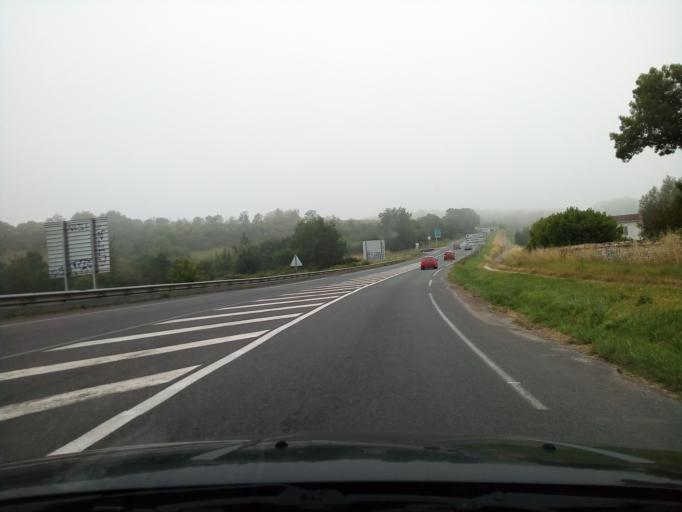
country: FR
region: Poitou-Charentes
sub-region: Departement de la Charente-Maritime
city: Cherac
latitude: 45.6884
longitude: -0.3985
